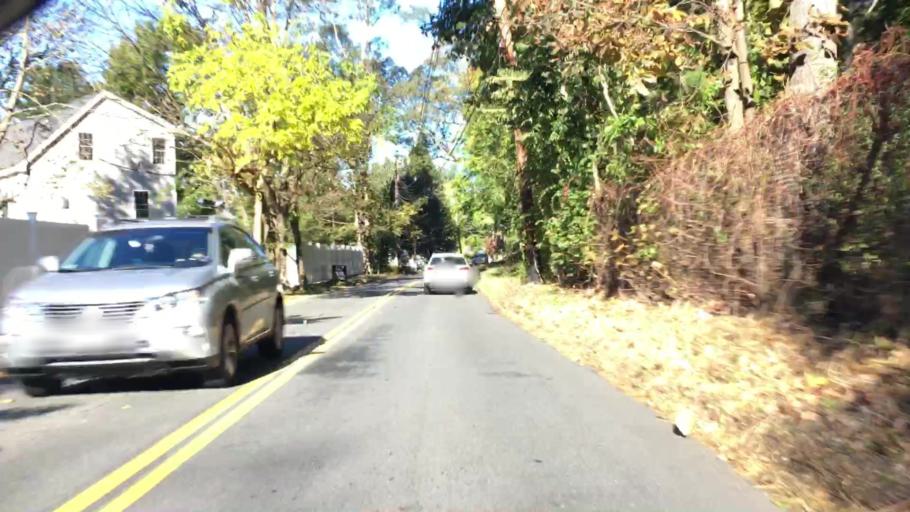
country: US
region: Massachusetts
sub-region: Middlesex County
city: Framingham Center
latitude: 42.2905
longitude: -71.4627
